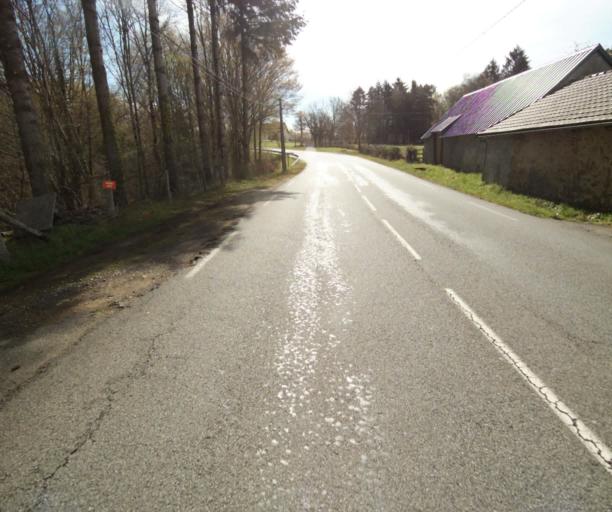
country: FR
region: Limousin
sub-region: Departement de la Correze
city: Laguenne
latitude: 45.2793
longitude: 1.8367
